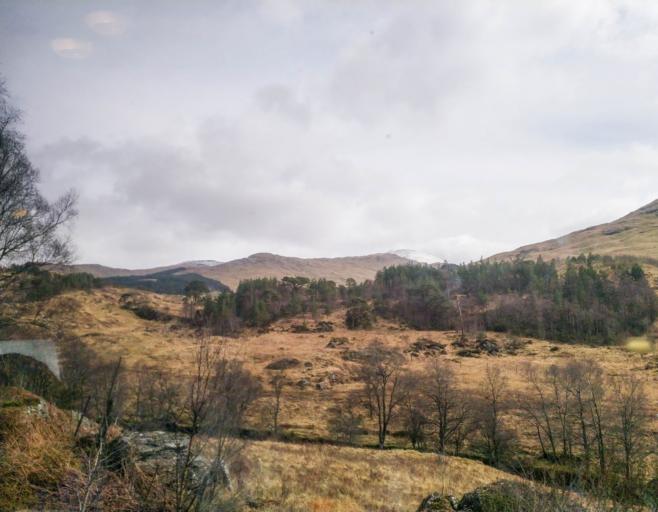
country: GB
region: Scotland
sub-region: Argyll and Bute
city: Garelochhead
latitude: 56.3725
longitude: -4.6526
